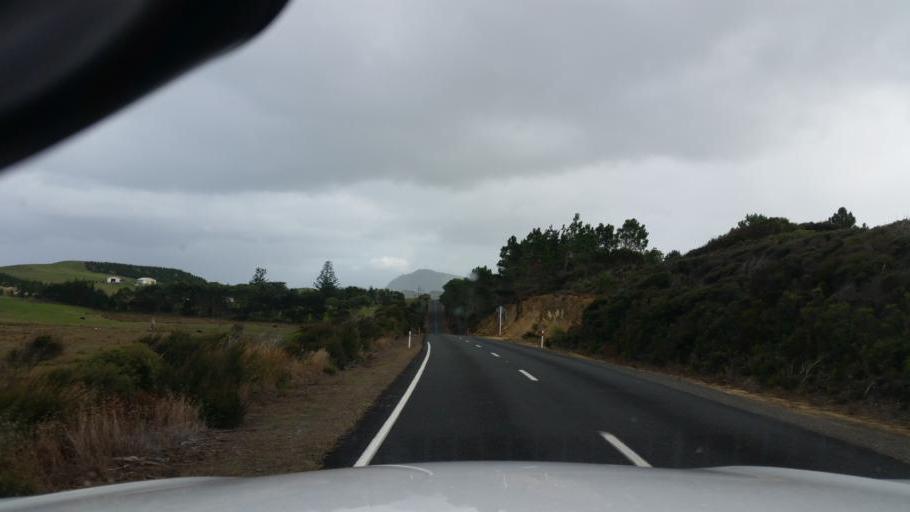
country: NZ
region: Northland
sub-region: Kaipara District
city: Dargaville
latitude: -35.8200
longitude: 173.6494
